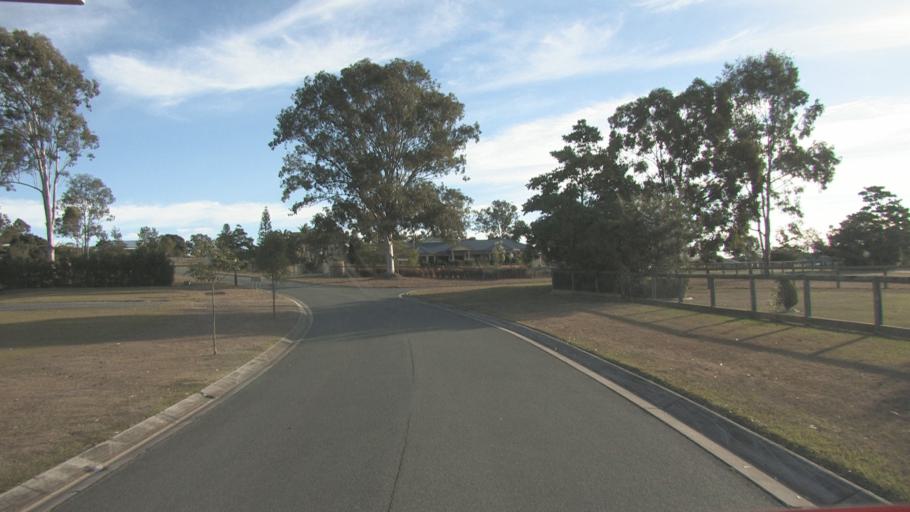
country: AU
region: Queensland
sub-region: Logan
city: North Maclean
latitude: -27.8285
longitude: 153.0066
